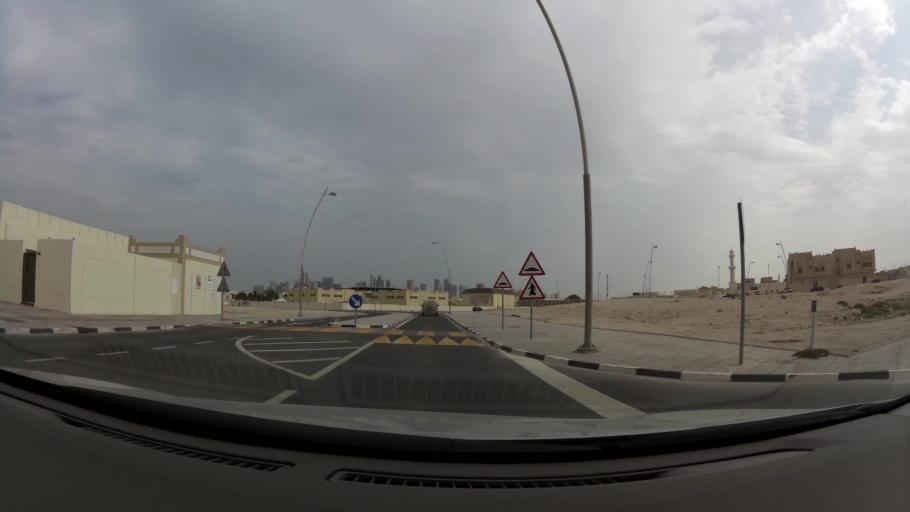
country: QA
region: Baladiyat ad Dawhah
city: Doha
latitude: 25.3448
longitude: 51.4992
